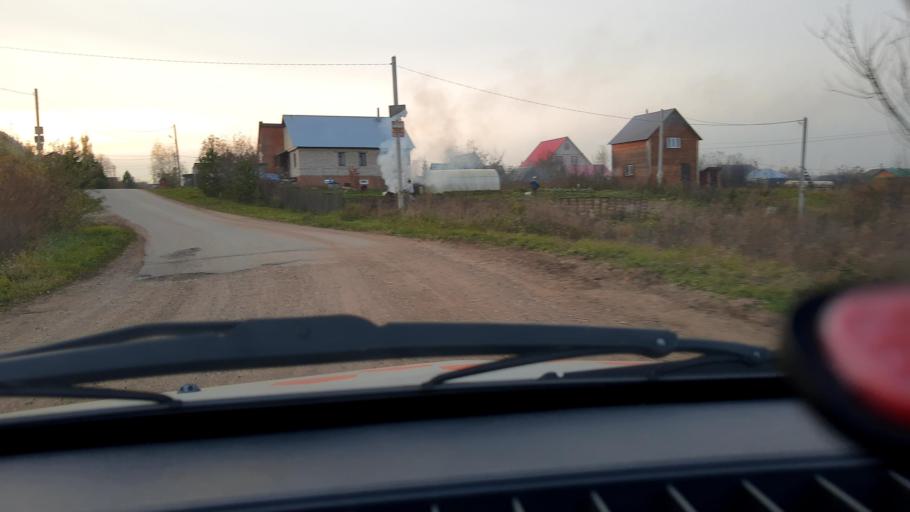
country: RU
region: Bashkortostan
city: Iglino
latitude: 54.7924
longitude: 56.3247
